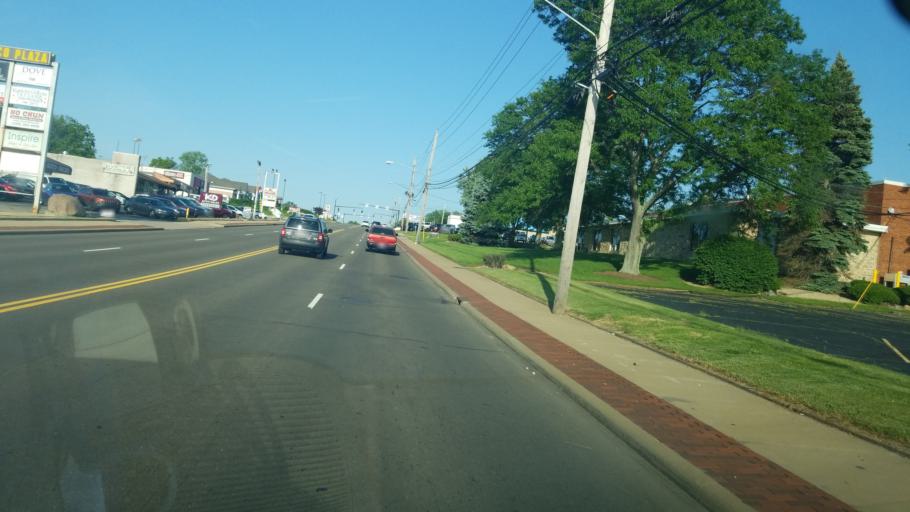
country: US
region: Ohio
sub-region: Summit County
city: Tallmadge
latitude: 41.1016
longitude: -81.4536
